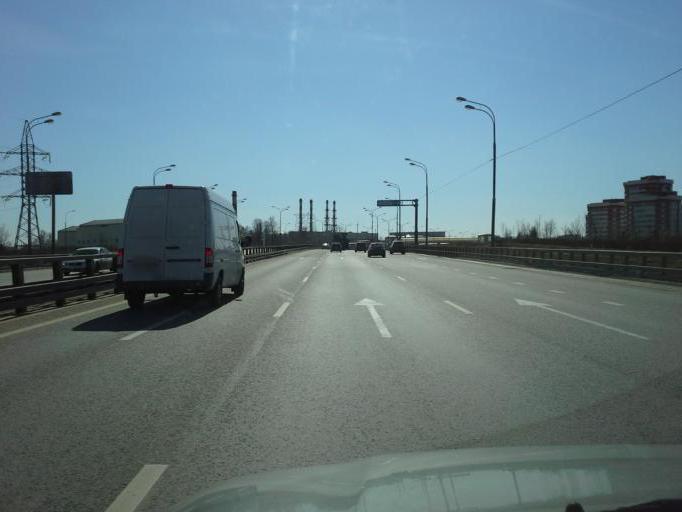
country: RU
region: Moskovskaya
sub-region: Leninskiy Rayon
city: Vnukovo
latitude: 55.6183
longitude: 37.2670
